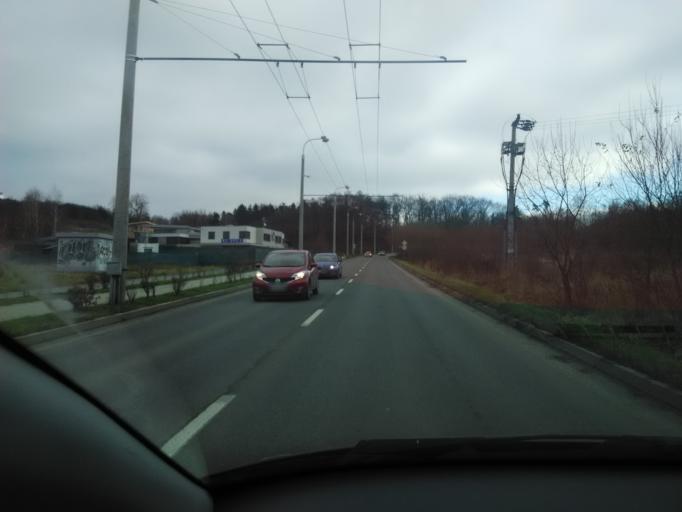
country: SK
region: Zilinsky
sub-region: Okres Zilina
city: Zilina
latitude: 49.2023
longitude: 18.7471
